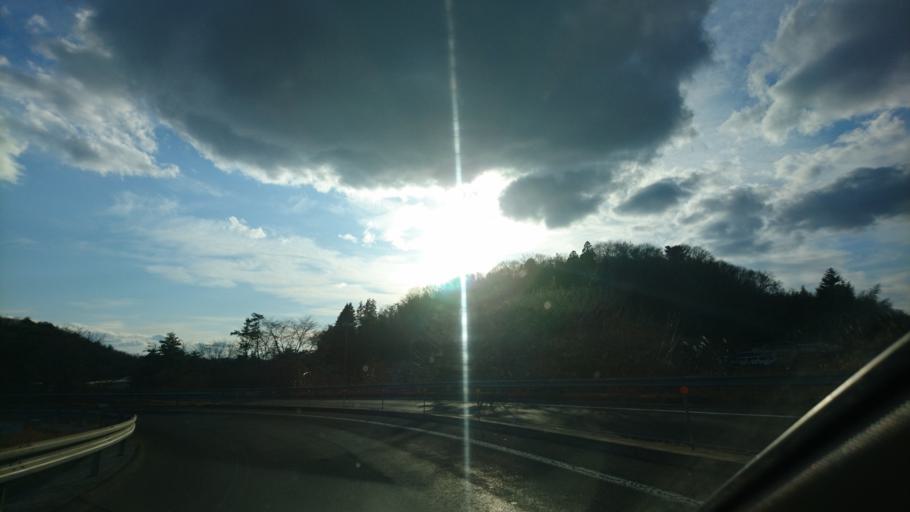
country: JP
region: Miyagi
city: Furukawa
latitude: 38.7113
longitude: 141.0081
